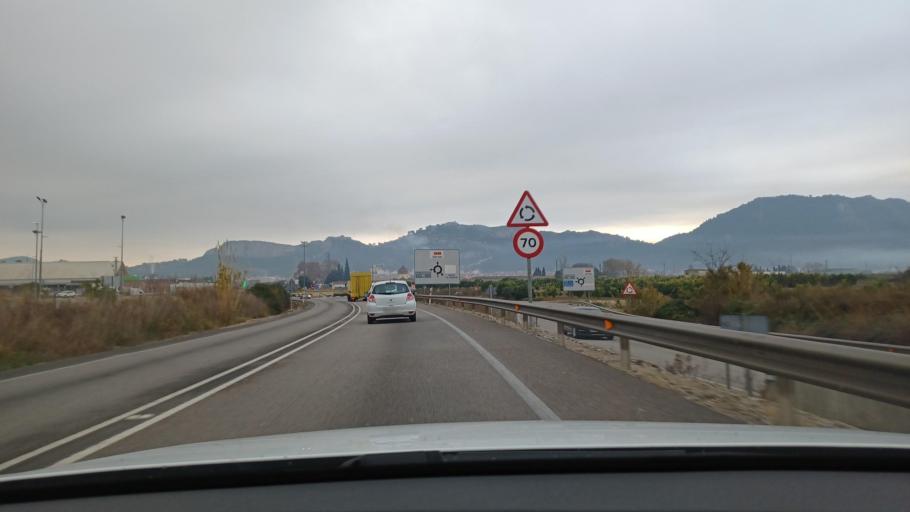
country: ES
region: Valencia
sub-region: Provincia de Valencia
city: Llosa de Ranes
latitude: 39.0035
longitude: -0.5301
